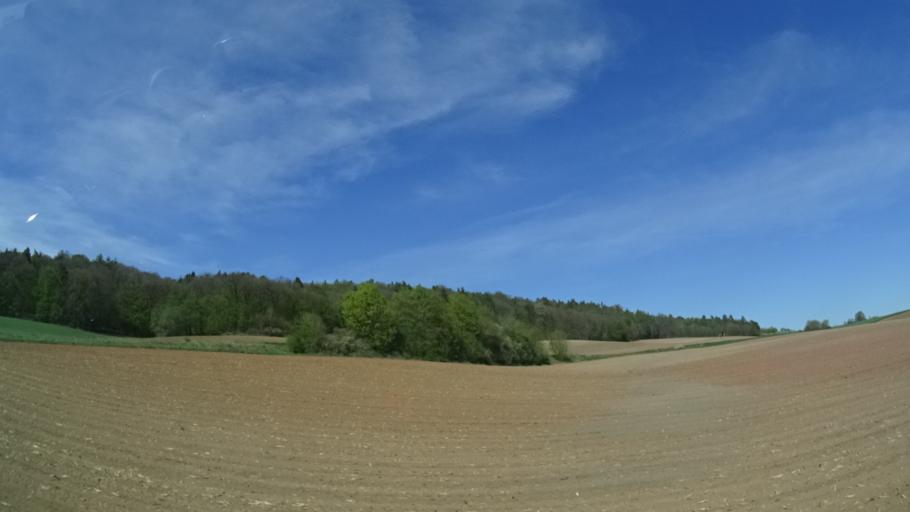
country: DE
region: Bavaria
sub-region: Regierungsbezirk Unterfranken
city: Burgpreppach
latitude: 50.1546
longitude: 10.6199
